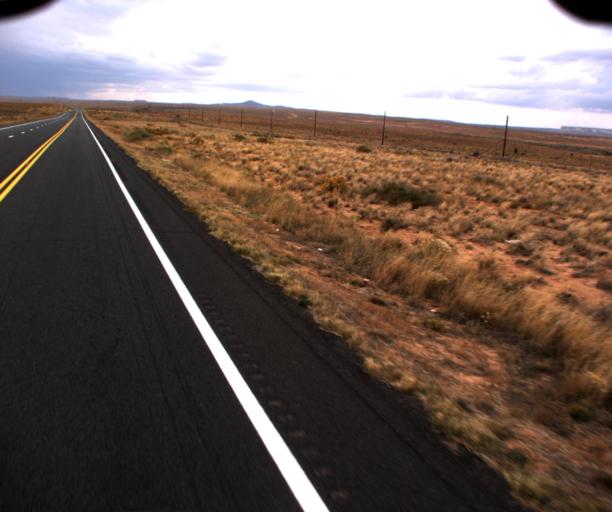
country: US
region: Arizona
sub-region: Coconino County
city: Kaibito
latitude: 36.3996
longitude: -110.8580
